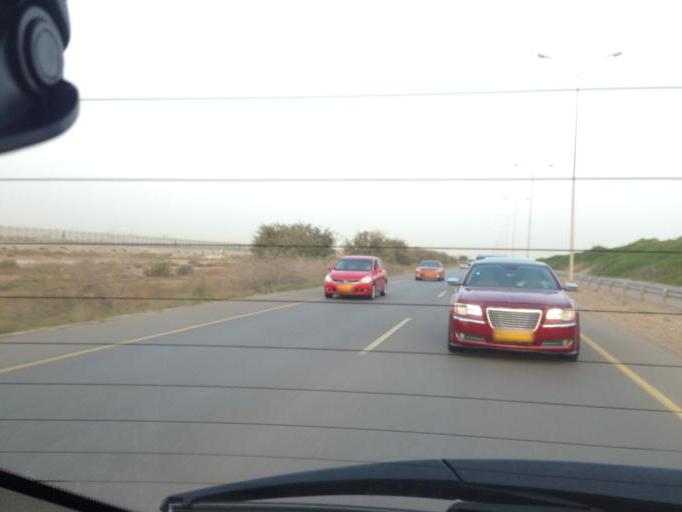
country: OM
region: Muhafazat Masqat
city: As Sib al Jadidah
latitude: 23.6154
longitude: 58.2890
